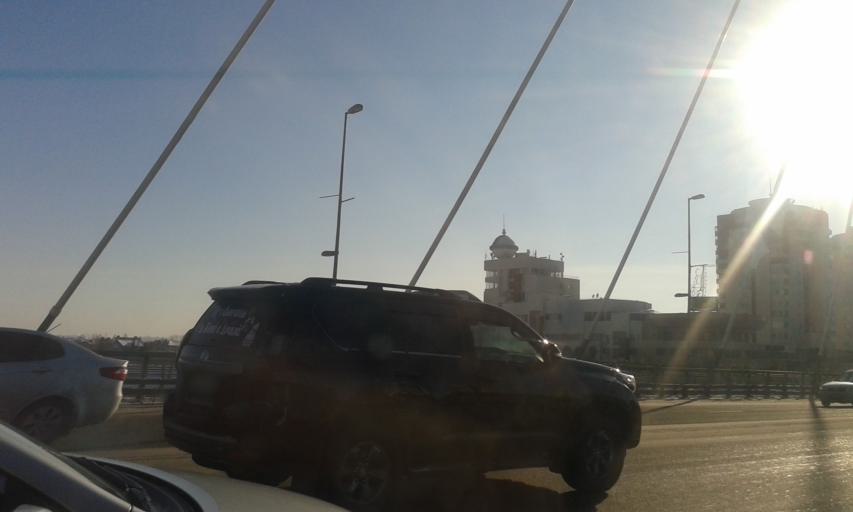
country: KZ
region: Astana Qalasy
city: Astana
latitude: 51.1523
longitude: 71.4283
